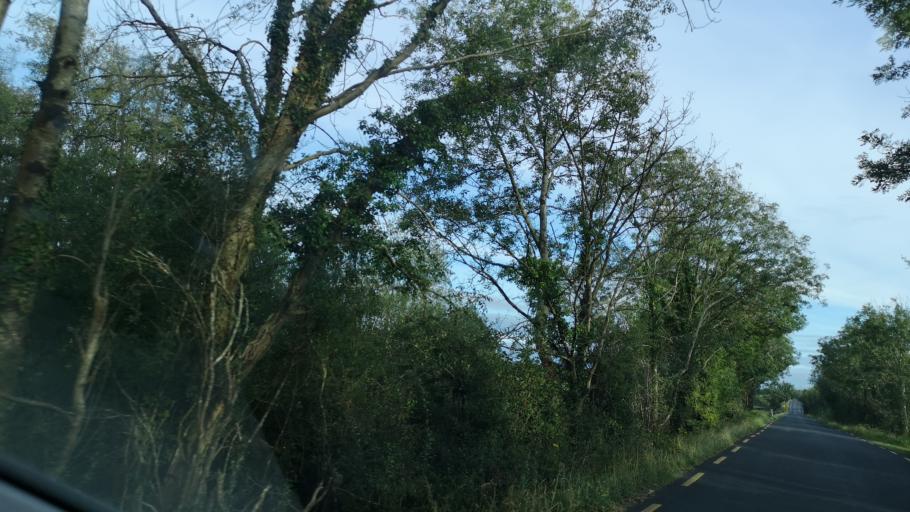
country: IE
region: Connaught
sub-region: County Galway
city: Ballinasloe
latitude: 53.3349
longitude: -8.2853
